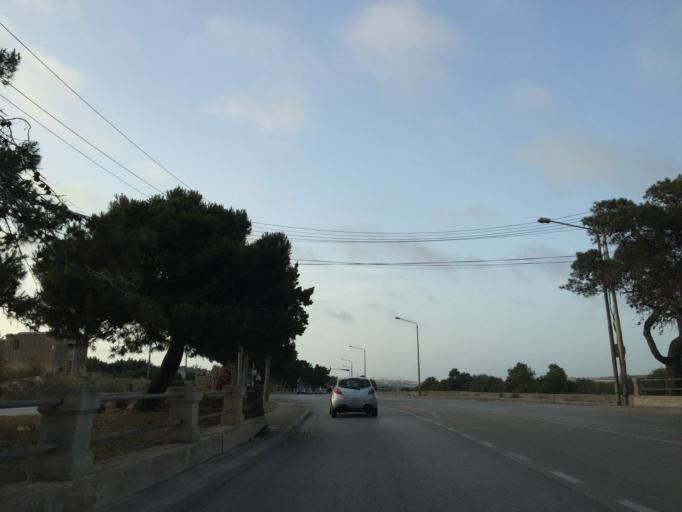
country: MT
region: Il-Mosta
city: Mosta
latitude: 35.9242
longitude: 14.4158
